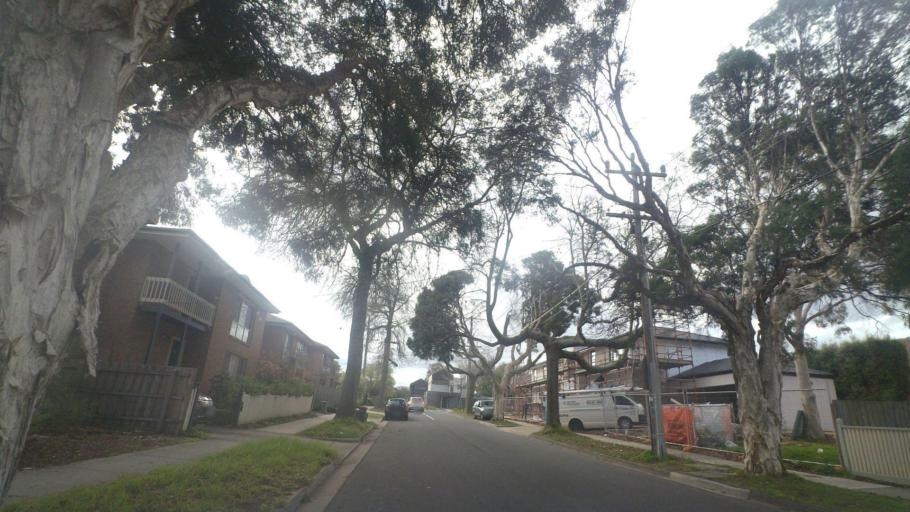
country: AU
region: Victoria
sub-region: Whitehorse
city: Blackburn North
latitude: -37.8119
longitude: 145.1599
